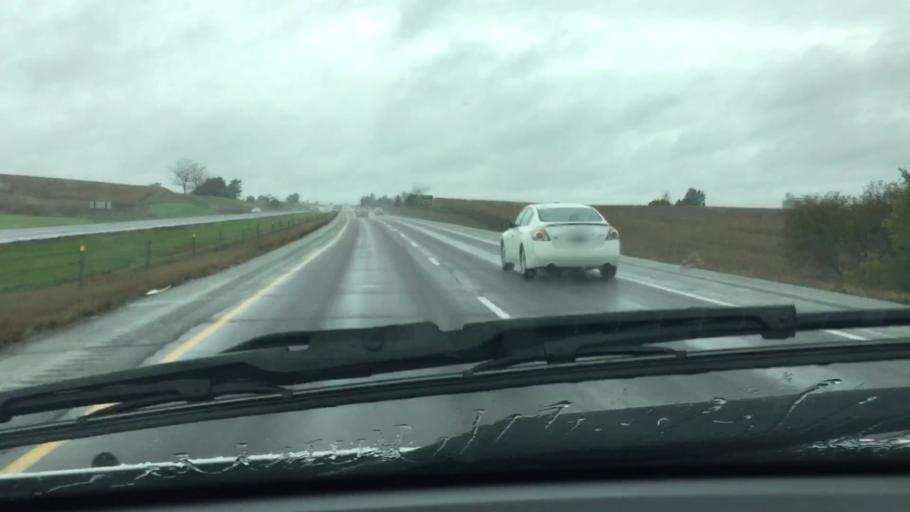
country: US
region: Iowa
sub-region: Poweshiek County
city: Brooklyn
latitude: 41.6964
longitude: -92.5326
